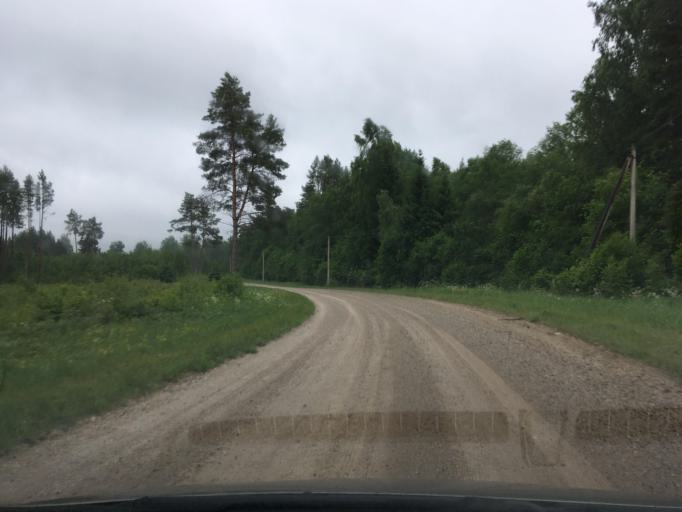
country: EE
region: Laeaene
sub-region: Lihula vald
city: Lihula
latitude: 58.6496
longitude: 23.7751
